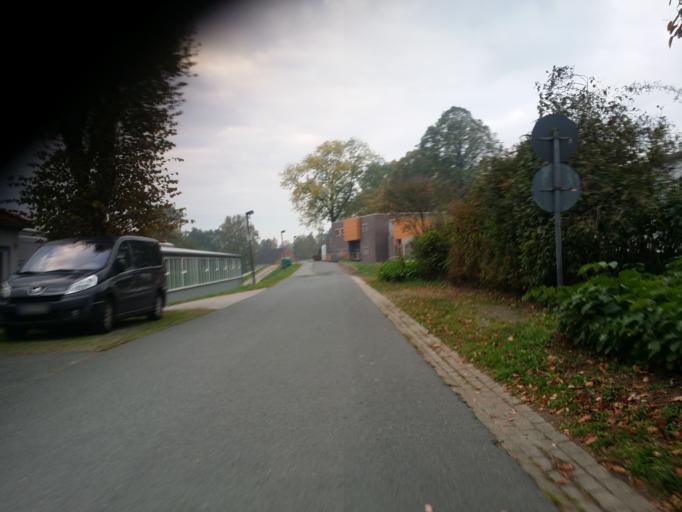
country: DE
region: Lower Saxony
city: Ritterhude
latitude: 53.1601
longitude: 8.7096
